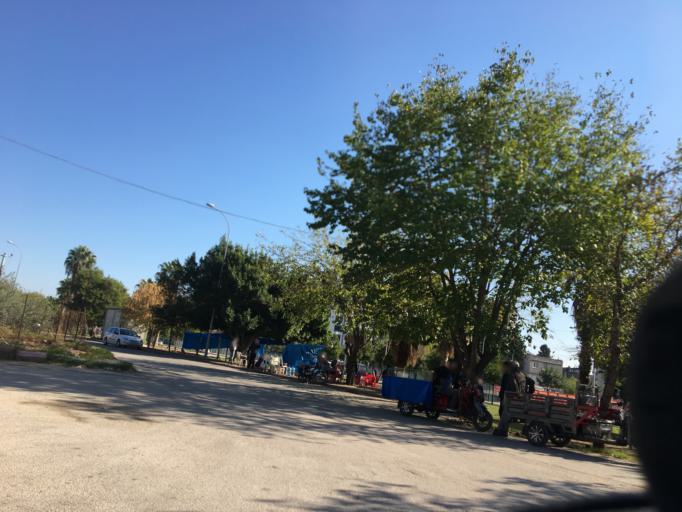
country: TR
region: Adana
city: Seyhan
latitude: 37.0117
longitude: 35.2932
